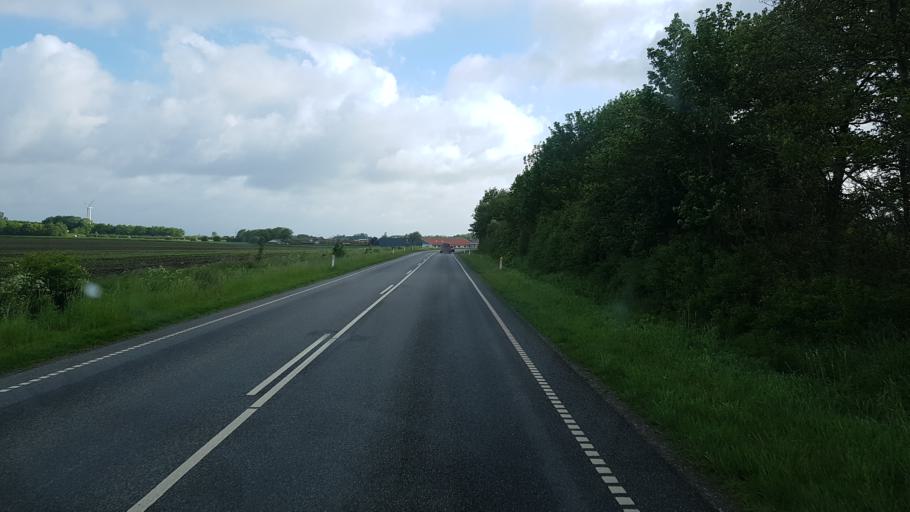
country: DK
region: South Denmark
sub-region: Vejen Kommune
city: Vejen
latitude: 55.4177
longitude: 9.1382
